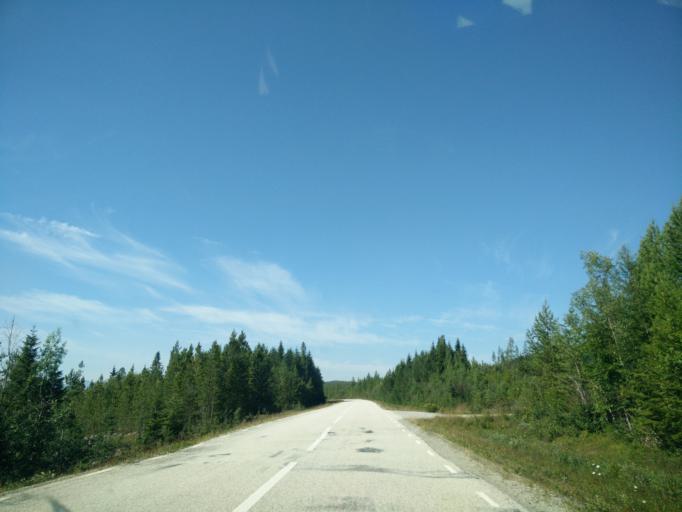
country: SE
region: Jaemtland
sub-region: Are Kommun
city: Jarpen
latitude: 62.8128
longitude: 13.5218
